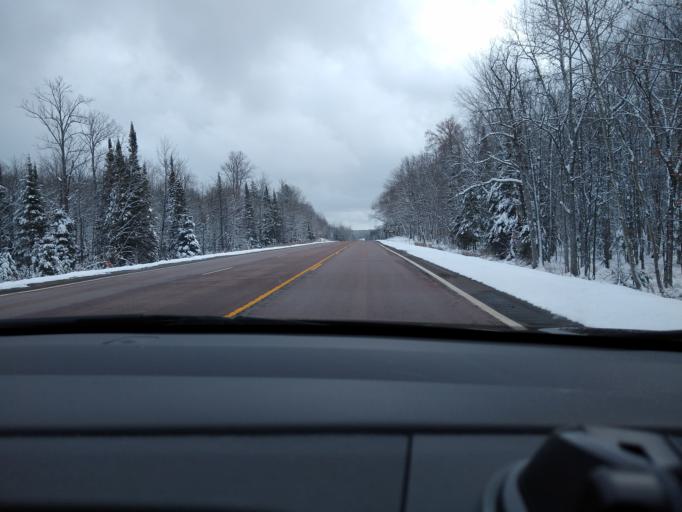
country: US
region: Wisconsin
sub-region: Vilas County
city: Eagle River
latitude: 46.2035
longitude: -89.0195
